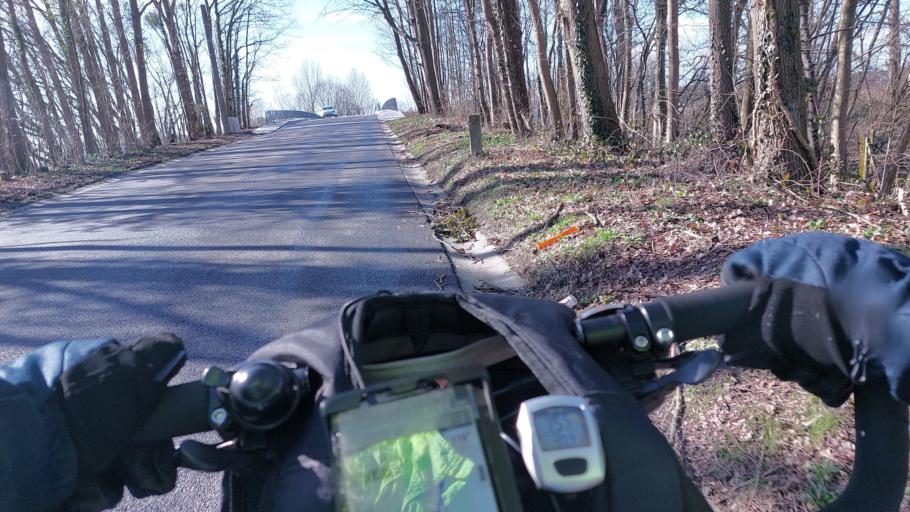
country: BE
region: Wallonia
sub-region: Province du Hainaut
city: Seneffe
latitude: 50.5564
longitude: 4.2249
